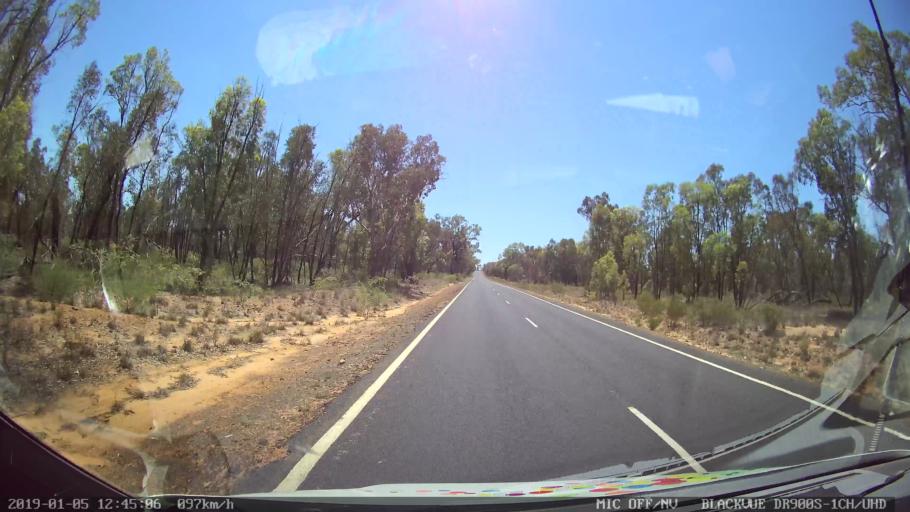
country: AU
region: New South Wales
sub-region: Warrumbungle Shire
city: Coonabarabran
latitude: -31.1311
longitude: 149.5458
